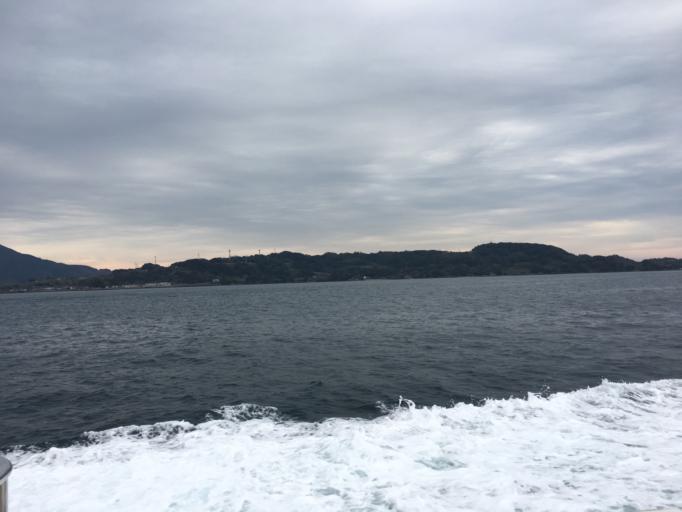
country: JP
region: Nagasaki
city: Nagasaki-shi
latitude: 32.7081
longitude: 129.8039
